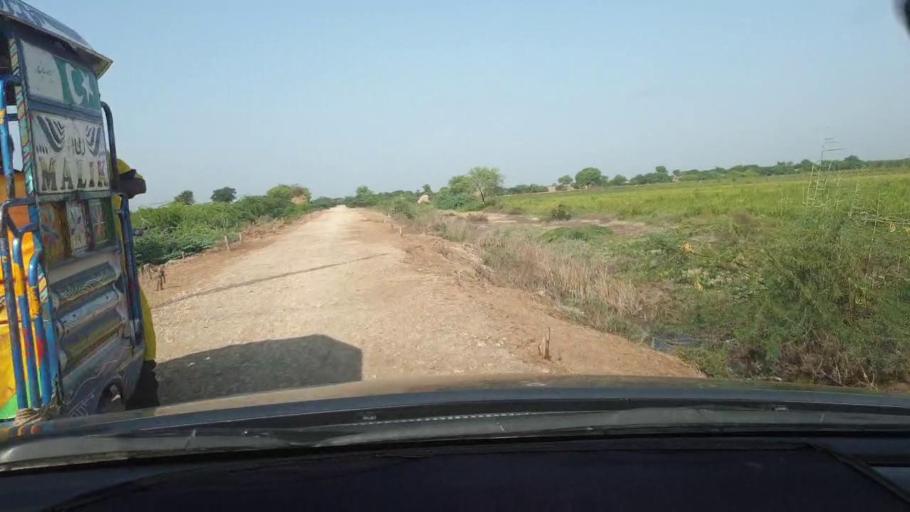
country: PK
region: Sindh
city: Tando Bago
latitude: 24.6800
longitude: 69.1498
